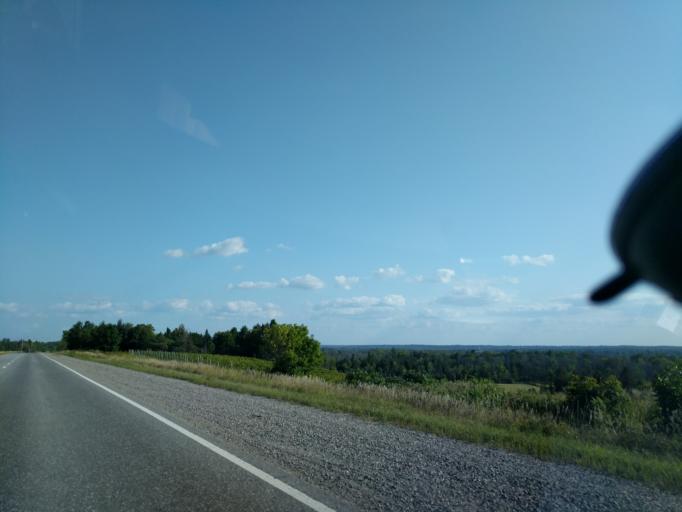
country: CA
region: Quebec
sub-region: Outaouais
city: Wakefield
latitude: 45.5192
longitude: -75.9869
